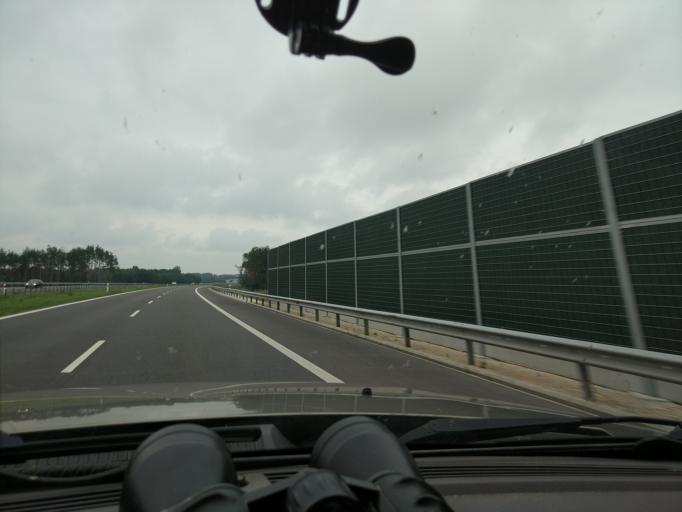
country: PL
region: Podlasie
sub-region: Powiat zambrowski
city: Szumowo
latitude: 52.8899
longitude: 22.0540
